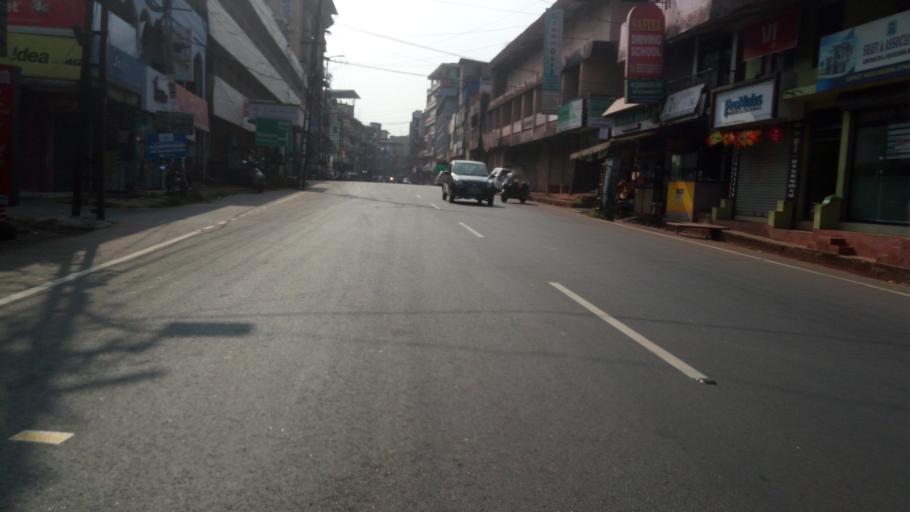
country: IN
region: Kerala
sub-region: Malappuram
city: Malappuram
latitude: 11.0020
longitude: 76.0085
